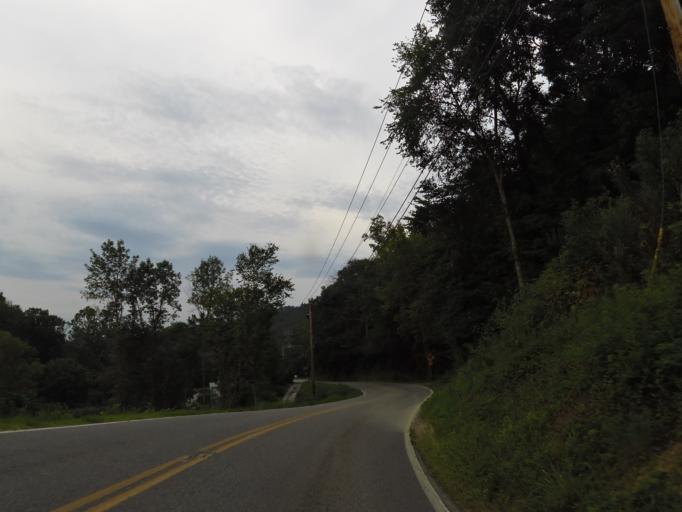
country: US
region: Tennessee
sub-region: Anderson County
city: Rocky Top
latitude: 36.2130
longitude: -84.1652
